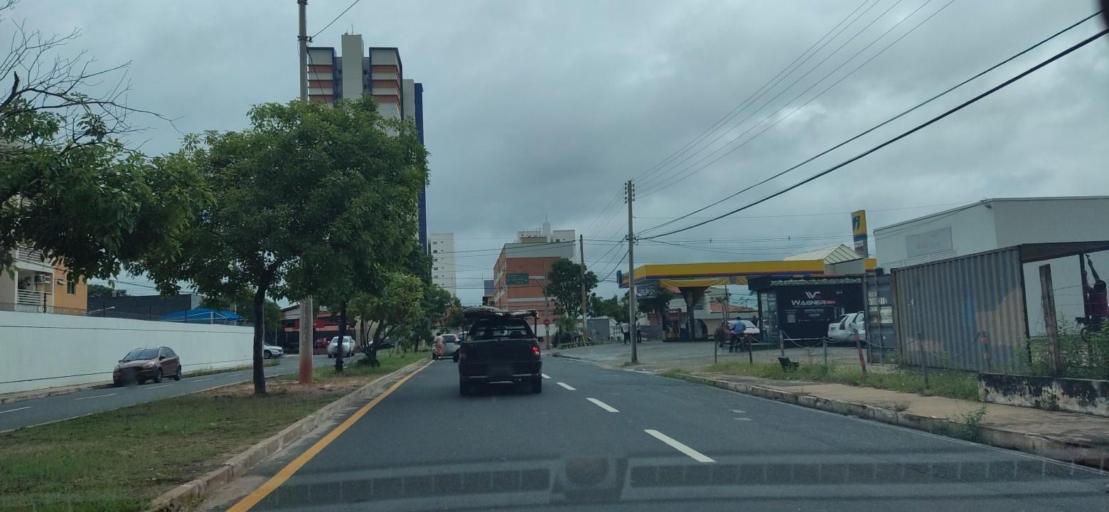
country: BR
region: Piaui
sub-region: Teresina
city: Teresina
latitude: -5.0704
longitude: -42.7502
